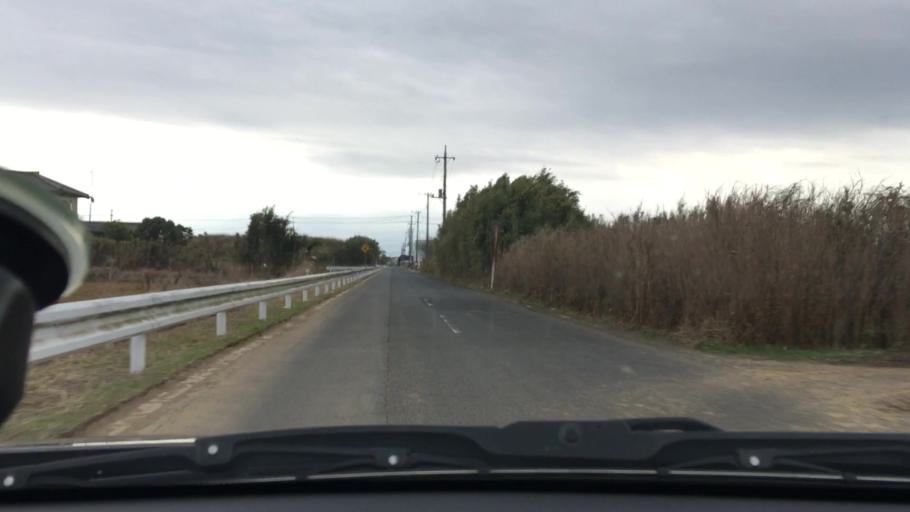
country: JP
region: Chiba
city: Omigawa
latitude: 35.8775
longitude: 140.6752
